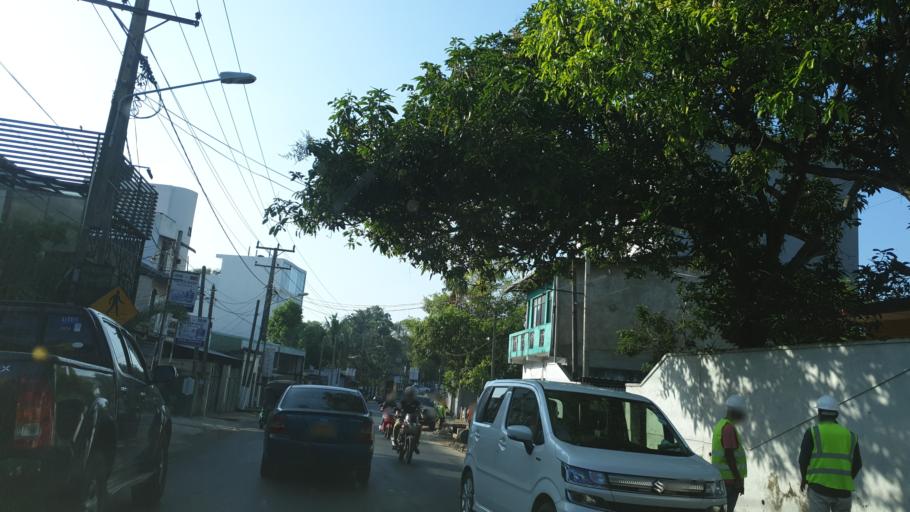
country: LK
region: Western
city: Sri Jayewardenepura Kotte
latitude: 6.8734
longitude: 79.9036
